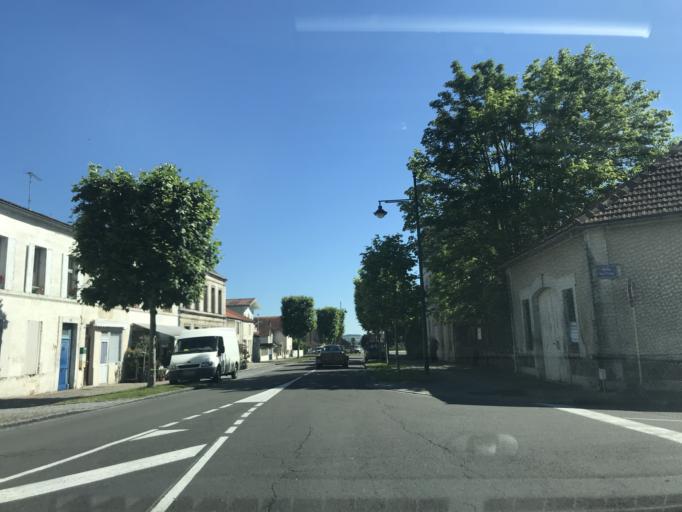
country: FR
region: Poitou-Charentes
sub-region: Departement de la Charente
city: Barbezieux-Saint-Hilaire
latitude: 45.4760
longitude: -0.1490
